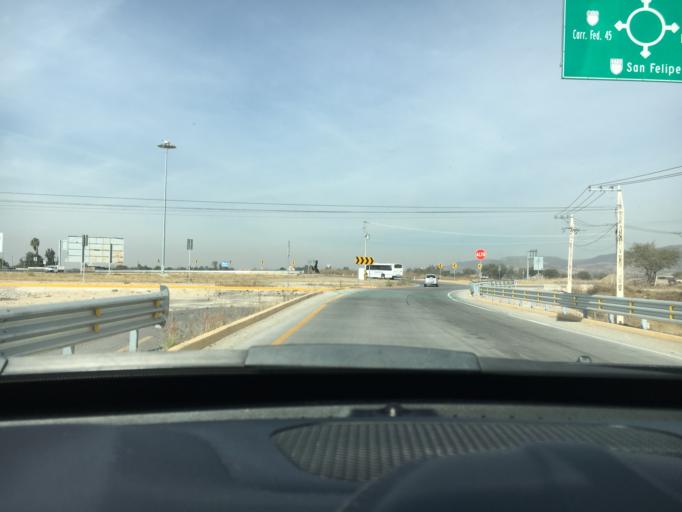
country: MX
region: Guanajuato
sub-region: Leon
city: Ladrilleras del Refugio
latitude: 21.0771
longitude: -101.5443
